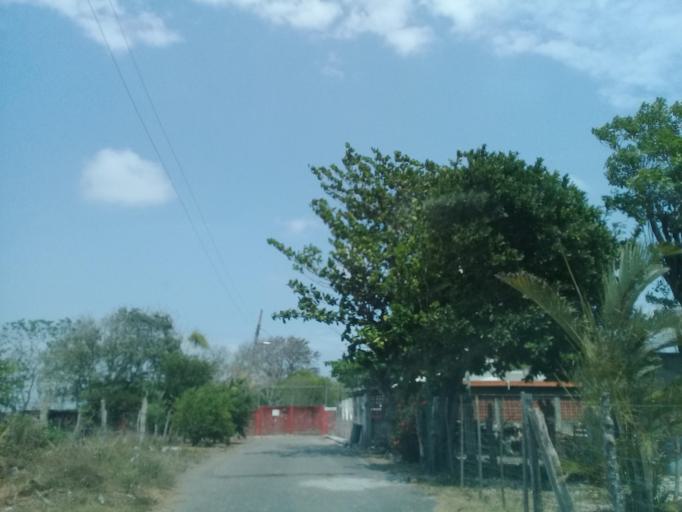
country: MX
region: Veracruz
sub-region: Veracruz
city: Delfino Victoria (Santa Fe)
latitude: 19.1747
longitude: -96.2749
